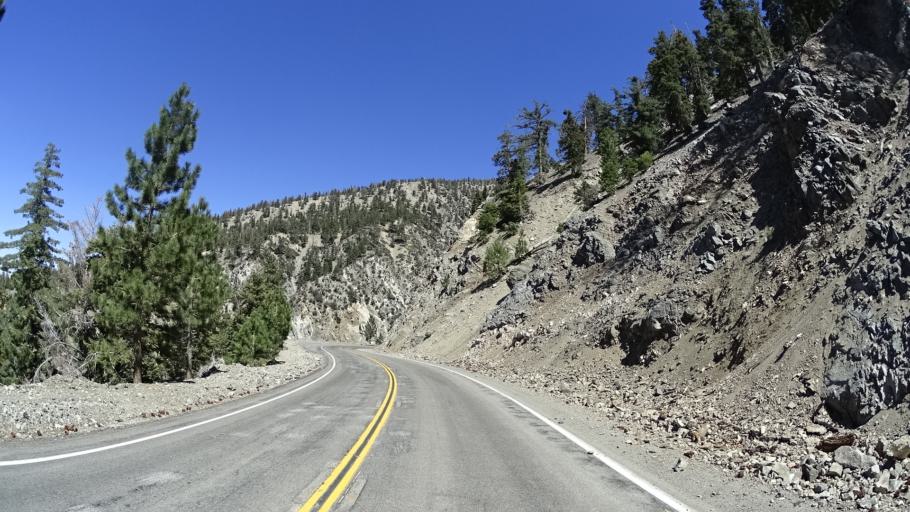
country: US
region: California
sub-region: San Bernardino County
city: Wrightwood
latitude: 34.3681
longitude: -117.7860
